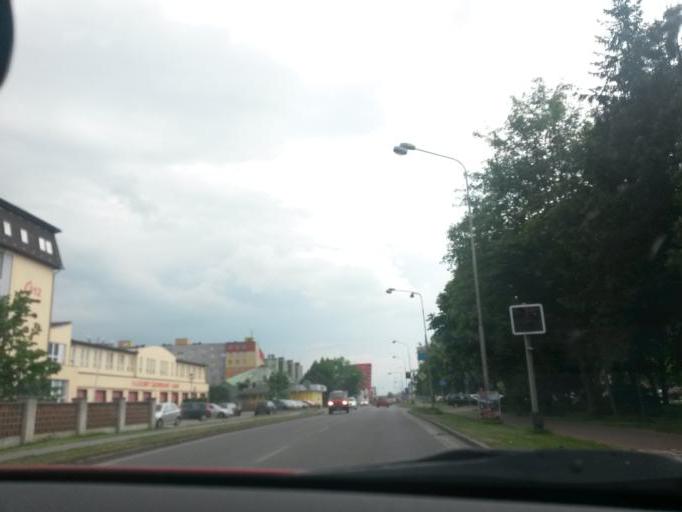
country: CZ
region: Olomoucky
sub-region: Okres Olomouc
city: Olomouc
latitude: 49.5785
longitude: 17.2486
